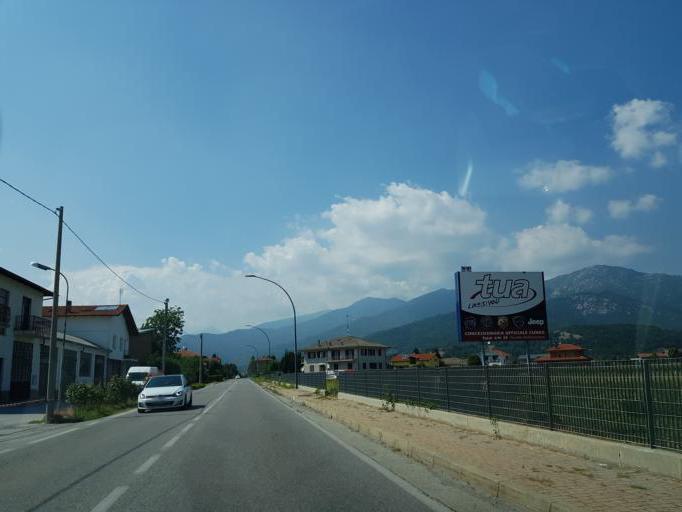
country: IT
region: Piedmont
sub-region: Provincia di Cuneo
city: Dronero
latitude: 44.4577
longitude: 7.3786
